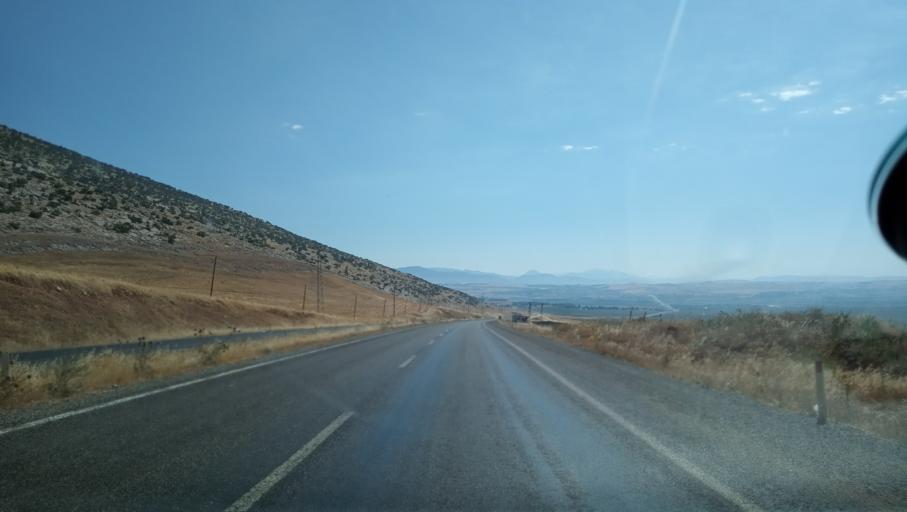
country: TR
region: Diyarbakir
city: Malabadi
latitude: 38.1247
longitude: 41.1607
